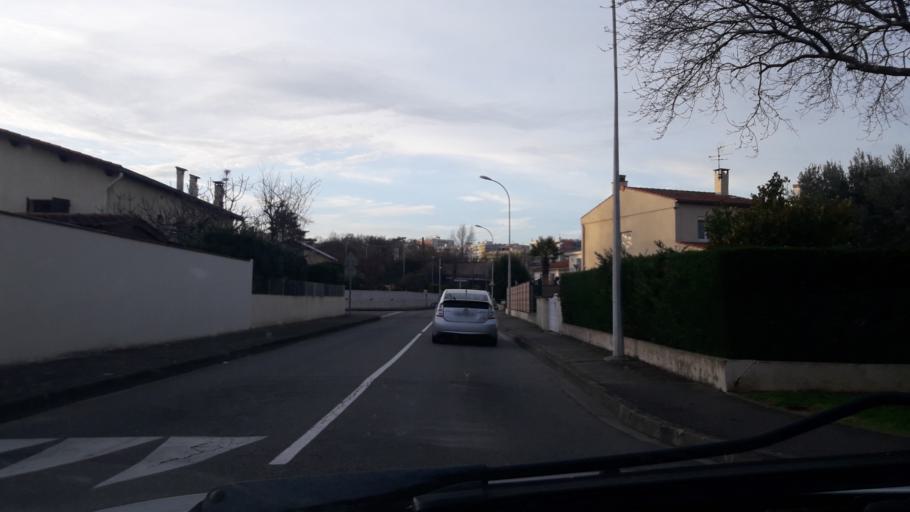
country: FR
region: Midi-Pyrenees
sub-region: Departement de la Haute-Garonne
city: Colomiers
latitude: 43.6046
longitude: 1.3486
